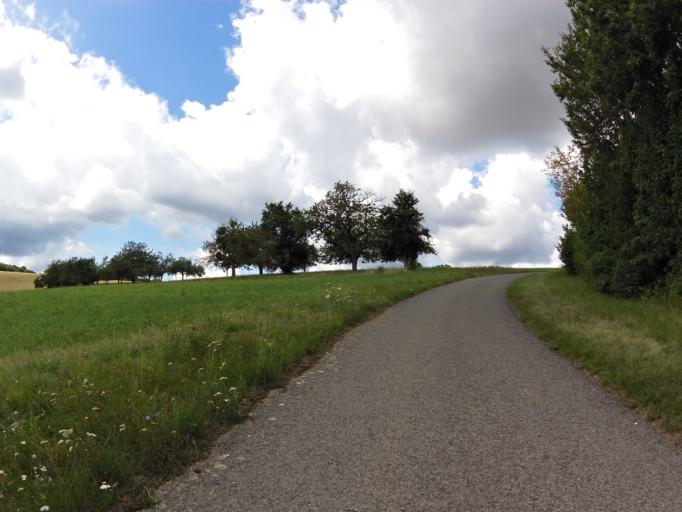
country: DE
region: Bavaria
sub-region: Regierungsbezirk Unterfranken
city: Margetshochheim
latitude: 49.8337
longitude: 9.8527
